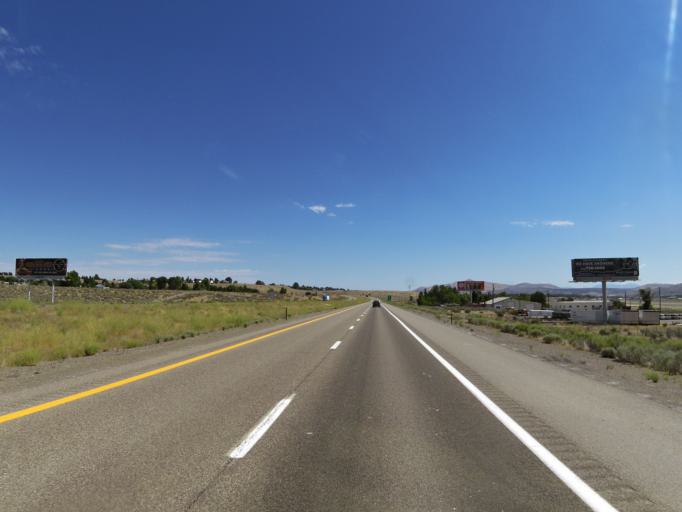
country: US
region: Nevada
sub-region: Elko County
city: Elko
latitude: 40.8202
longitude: -115.8115
